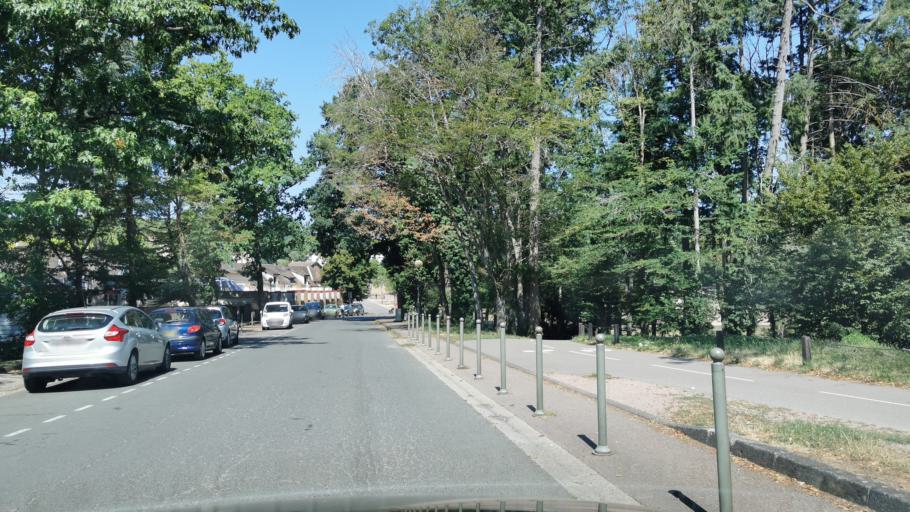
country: FR
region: Bourgogne
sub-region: Departement de Saone-et-Loire
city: Le Creusot
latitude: 46.8009
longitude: 4.4219
